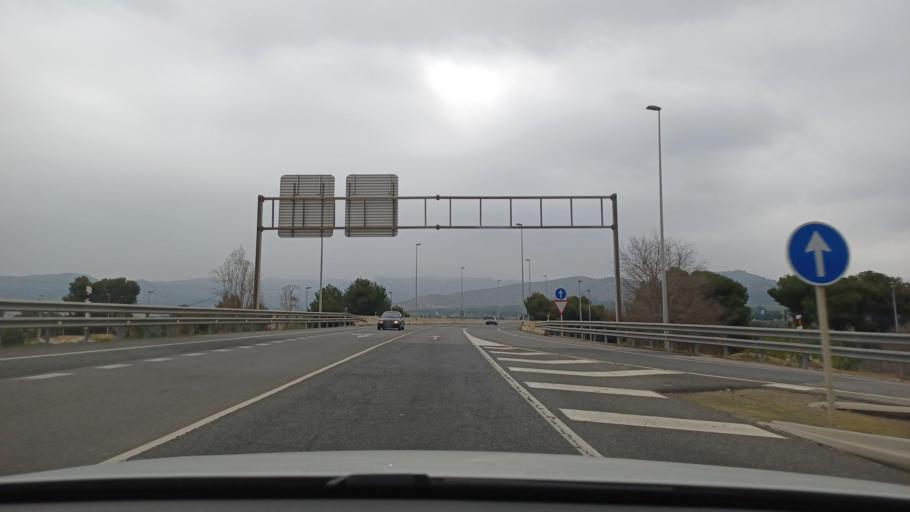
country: ES
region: Valencia
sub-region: Provincia de Castello
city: Borriol
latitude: 39.9933
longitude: -0.0898
